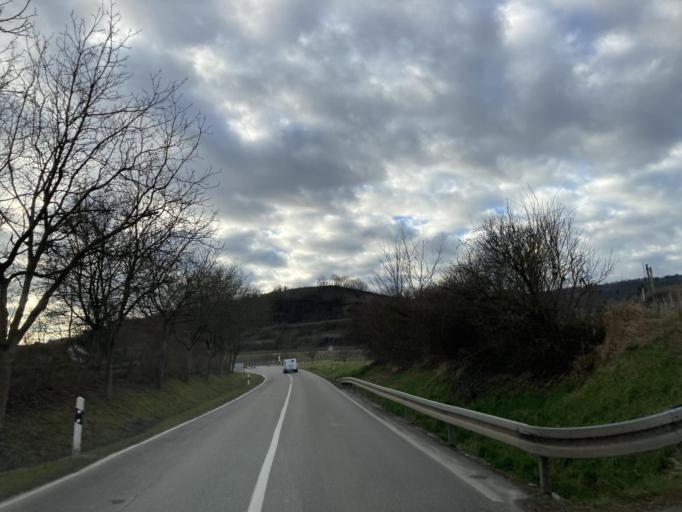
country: DE
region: Baden-Wuerttemberg
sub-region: Freiburg Region
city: Botzingen
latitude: 48.0681
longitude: 7.7111
